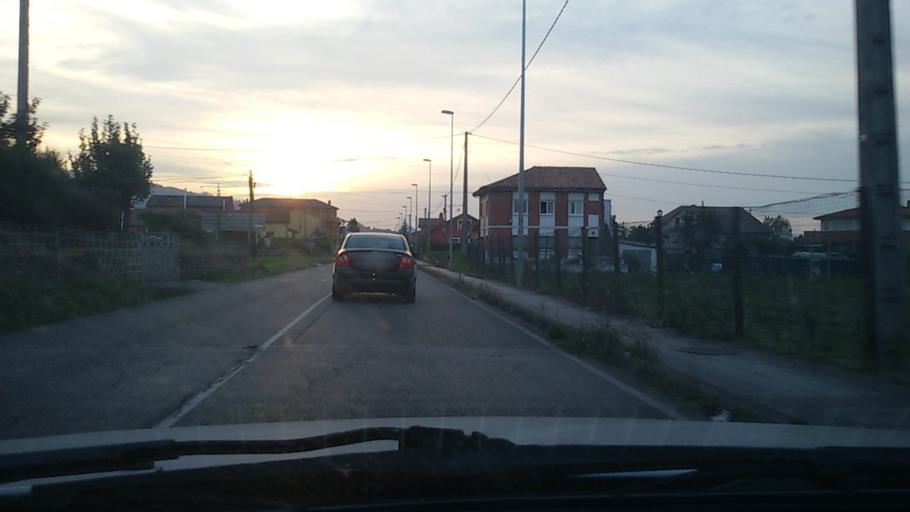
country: ES
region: Asturias
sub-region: Province of Asturias
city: Lugones
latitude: 43.3995
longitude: -5.7917
